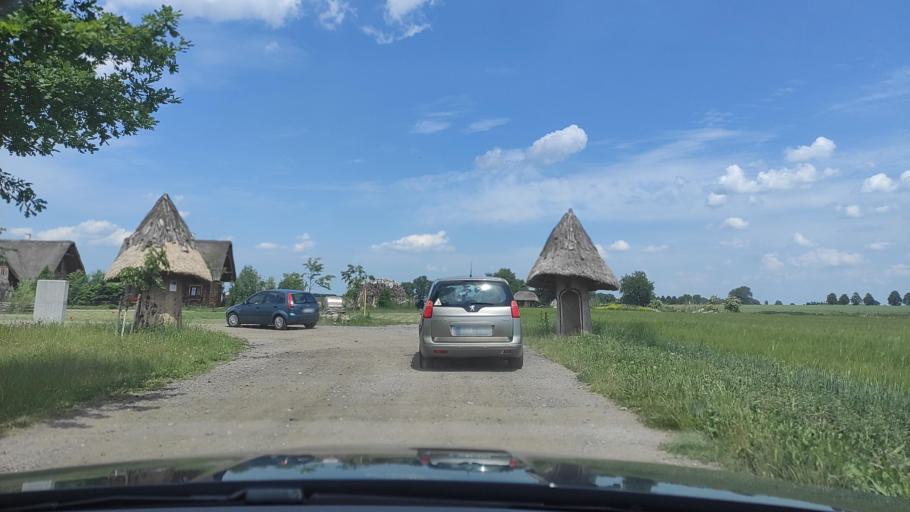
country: PL
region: Greater Poland Voivodeship
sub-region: Powiat gnieznienski
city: Lubowo
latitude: 52.5292
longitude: 17.3861
